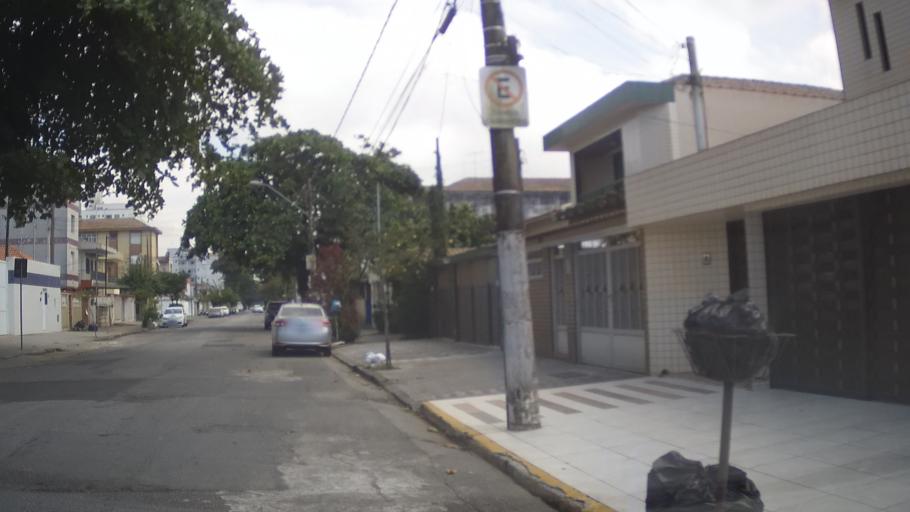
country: BR
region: Sao Paulo
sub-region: Santos
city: Santos
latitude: -23.9787
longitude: -46.2964
